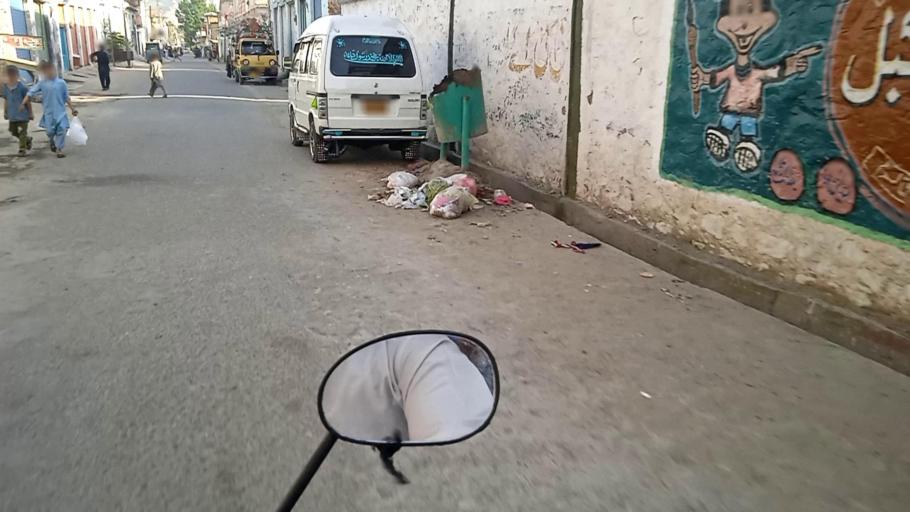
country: PK
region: Khyber Pakhtunkhwa
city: Mingora
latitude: 34.8139
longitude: 72.3591
